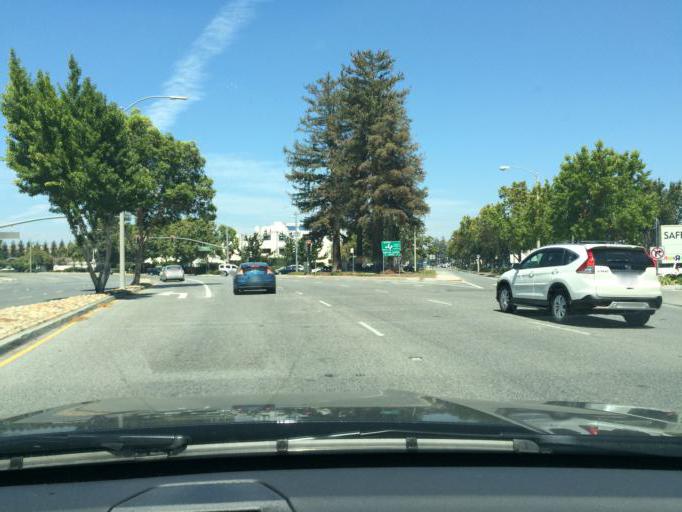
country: US
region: California
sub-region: Santa Clara County
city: Sunnyvale
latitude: 37.3635
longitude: -122.0323
